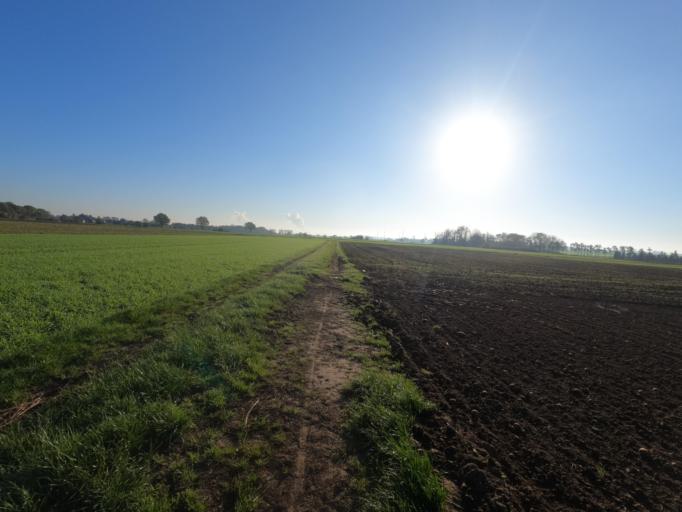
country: DE
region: North Rhine-Westphalia
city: Erkelenz
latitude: 51.0826
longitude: 6.3775
